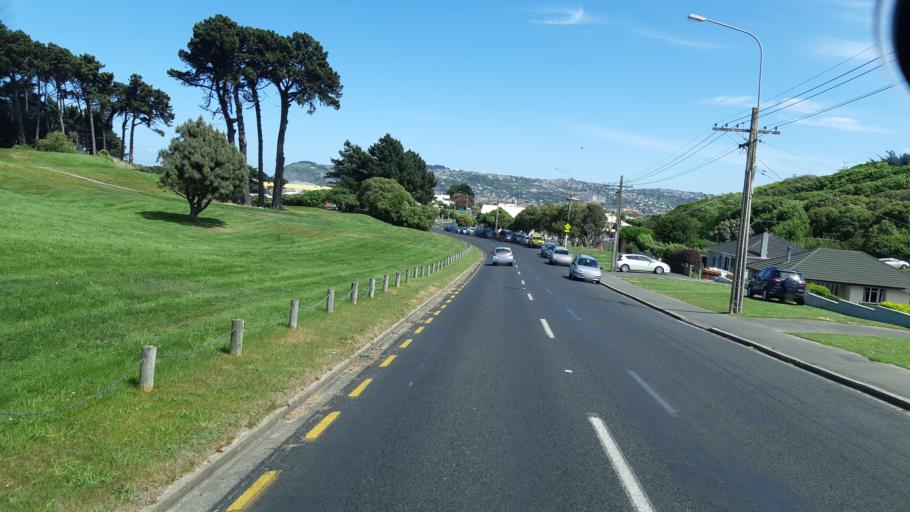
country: NZ
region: Otago
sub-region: Dunedin City
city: Dunedin
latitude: -45.9029
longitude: 170.5277
